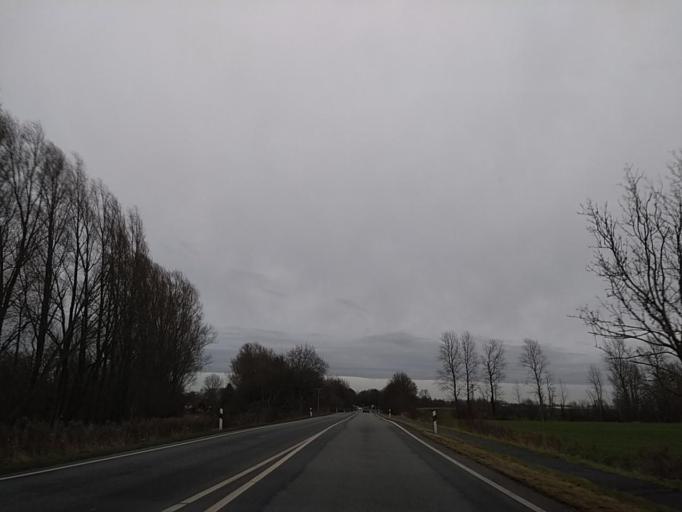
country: DE
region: Lower Saxony
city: Emden
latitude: 53.3618
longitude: 7.1411
